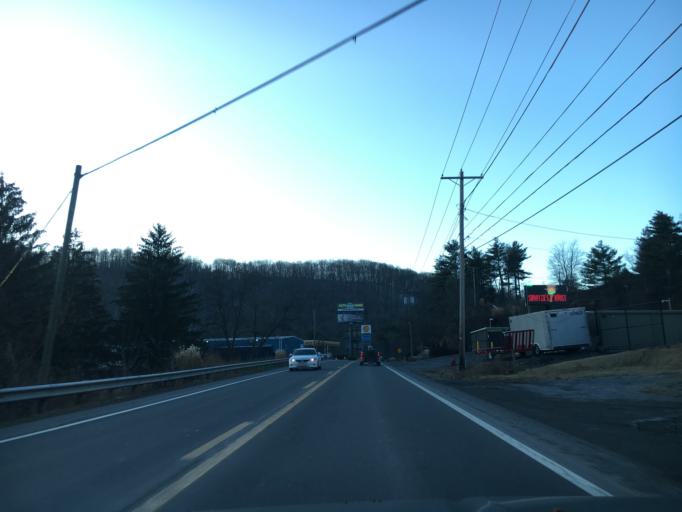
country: US
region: West Virginia
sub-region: Raleigh County
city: Daniels
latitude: 37.7294
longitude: -81.1099
